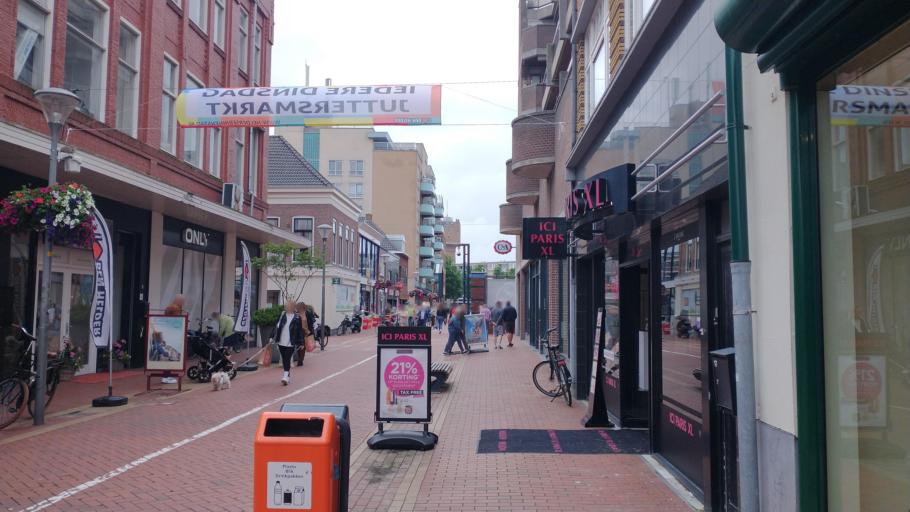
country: NL
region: North Holland
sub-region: Gemeente Den Helder
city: Den Helder
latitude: 52.9593
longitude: 4.7624
